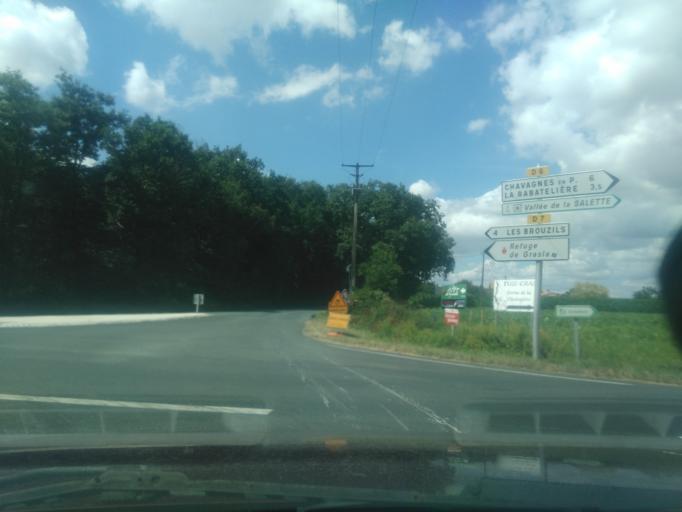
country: FR
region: Pays de la Loire
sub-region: Departement de la Vendee
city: Les Brouzils
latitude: 46.8538
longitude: -1.3020
